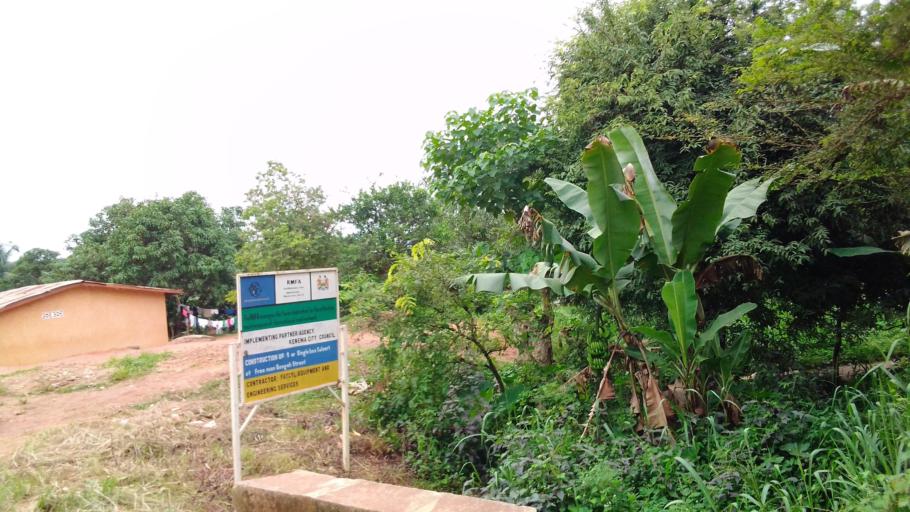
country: SL
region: Eastern Province
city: Kenema
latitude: 7.8611
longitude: -11.1841
